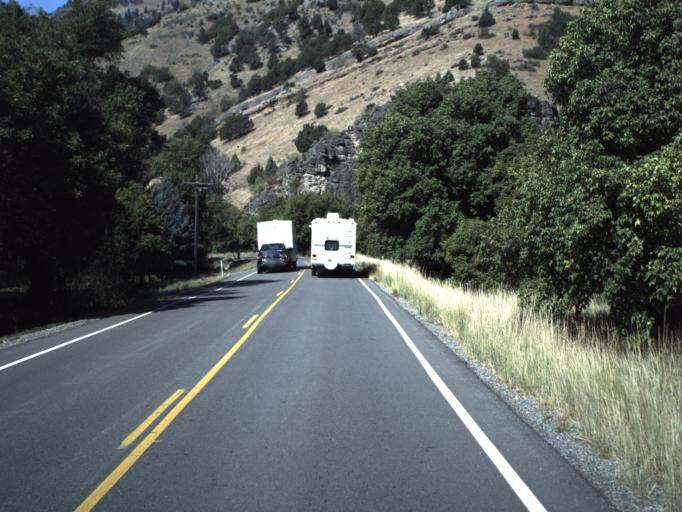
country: US
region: Utah
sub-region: Cache County
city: Millville
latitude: 41.6308
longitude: -111.7063
